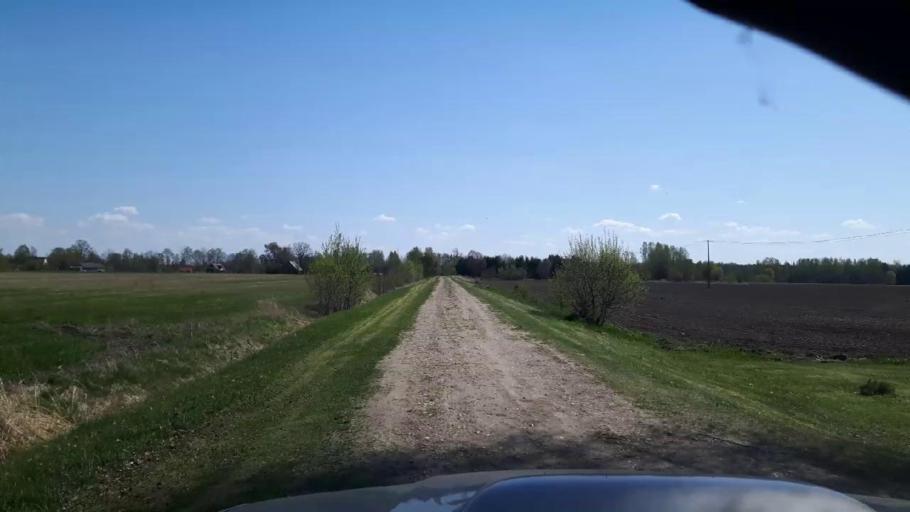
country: EE
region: Paernumaa
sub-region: Sindi linn
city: Sindi
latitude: 58.4620
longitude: 24.7559
